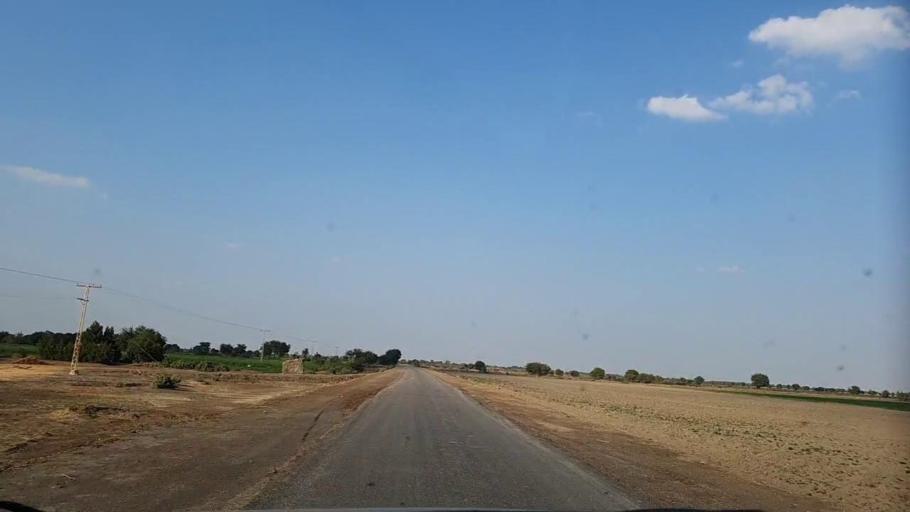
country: PK
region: Sindh
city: Pithoro
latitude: 25.6911
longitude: 69.2222
